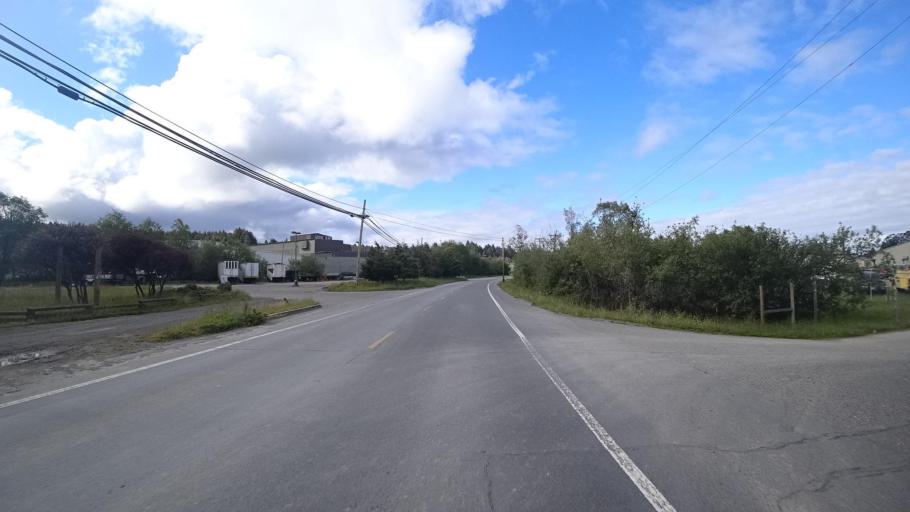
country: US
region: California
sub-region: Humboldt County
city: Arcata
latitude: 40.8993
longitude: -124.0748
